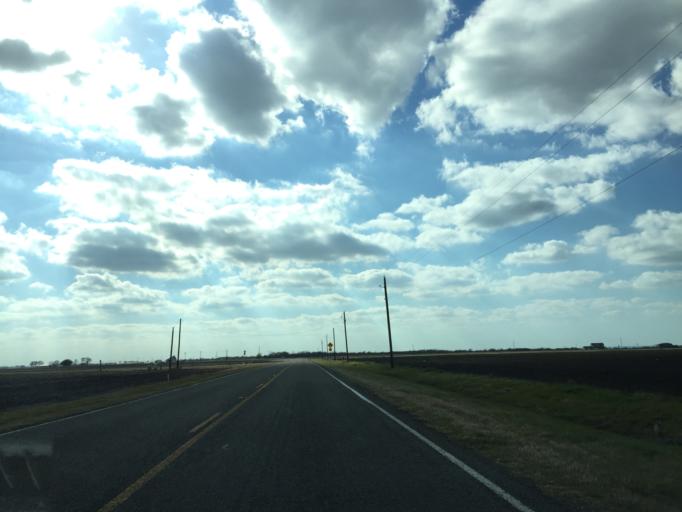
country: US
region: Texas
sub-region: Williamson County
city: Granger
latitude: 30.6743
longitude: -97.3482
